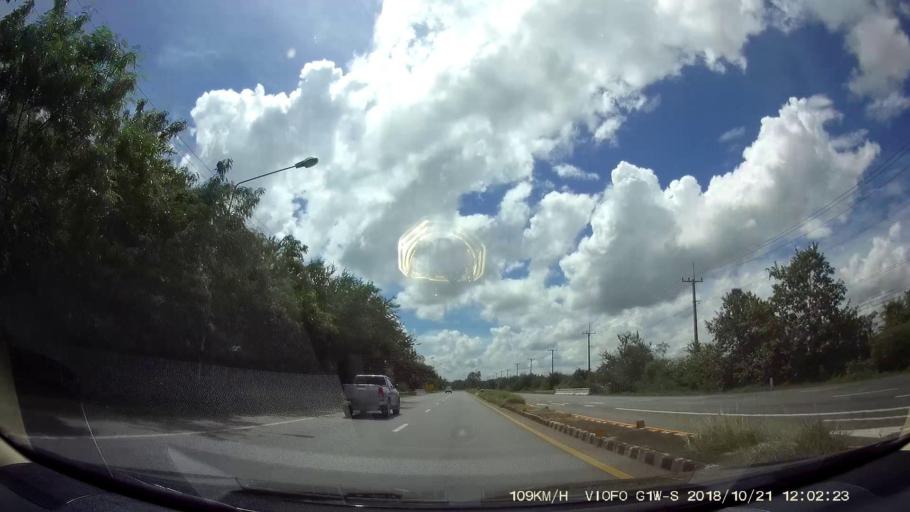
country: TH
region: Chaiyaphum
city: Chatturat
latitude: 15.5251
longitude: 101.8281
